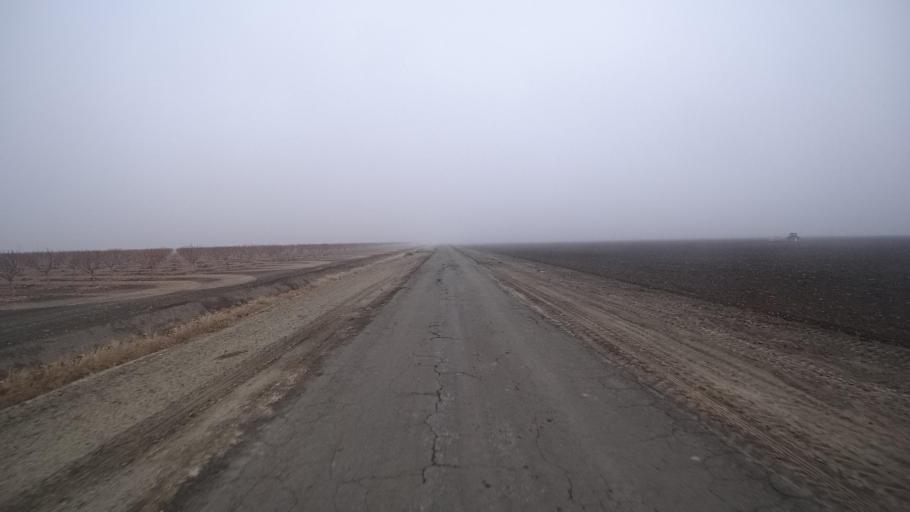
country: US
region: California
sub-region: Kern County
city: Buttonwillow
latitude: 35.4562
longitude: -119.5610
